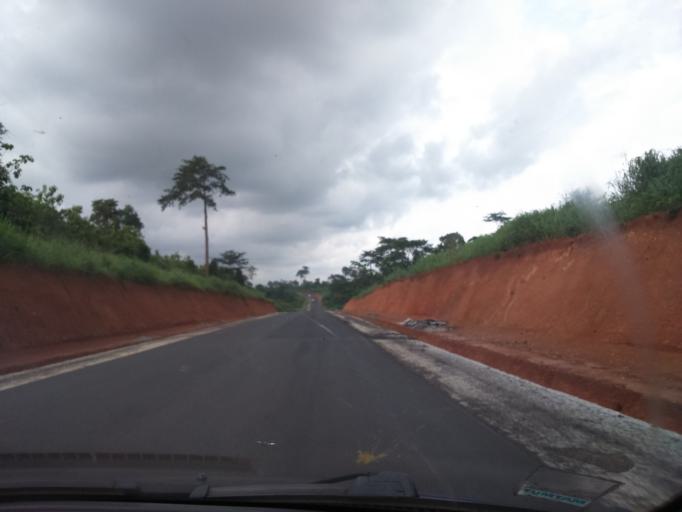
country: CI
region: Lagunes
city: Akoupe
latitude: 6.5047
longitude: -3.8213
